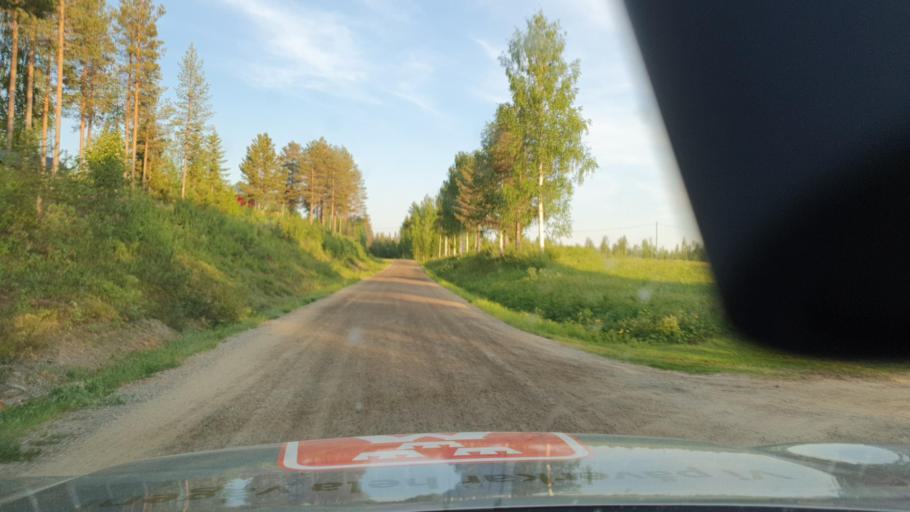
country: SE
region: Norrbotten
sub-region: Bodens Kommun
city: Boden
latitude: 66.1940
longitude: 21.4982
